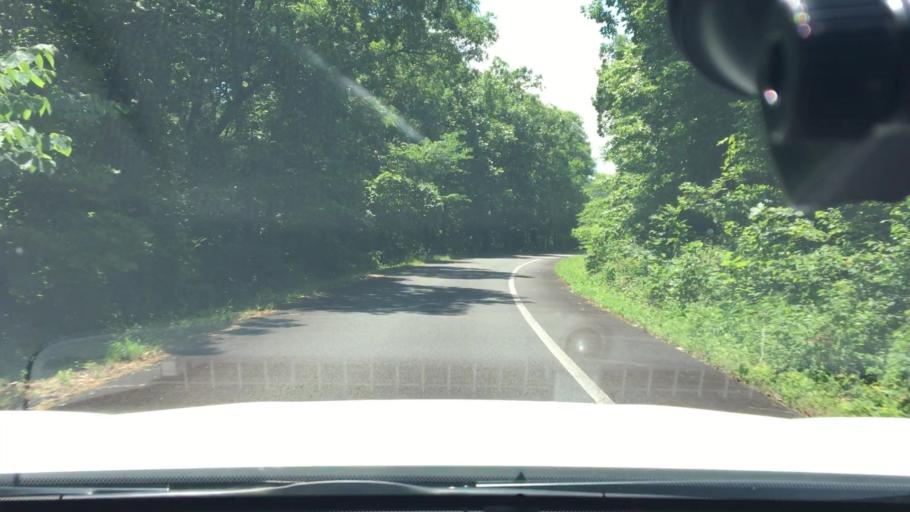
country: US
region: Arkansas
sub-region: Logan County
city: Paris
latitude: 35.1712
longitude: -93.6396
